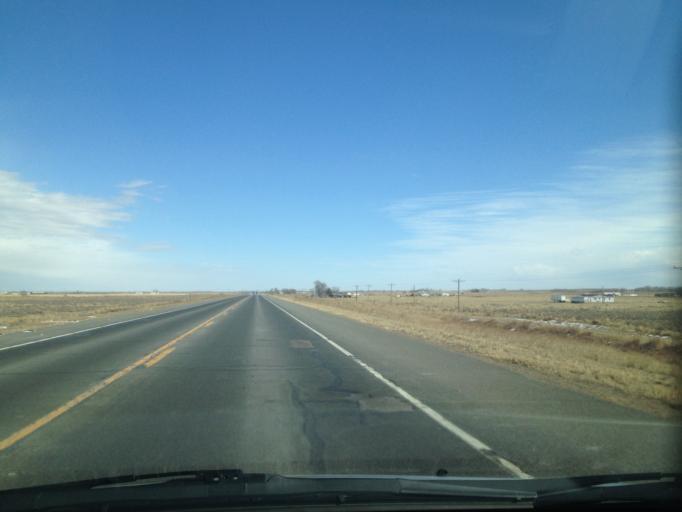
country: US
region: Colorado
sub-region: Weld County
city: Kersey
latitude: 40.2912
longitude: -104.2658
